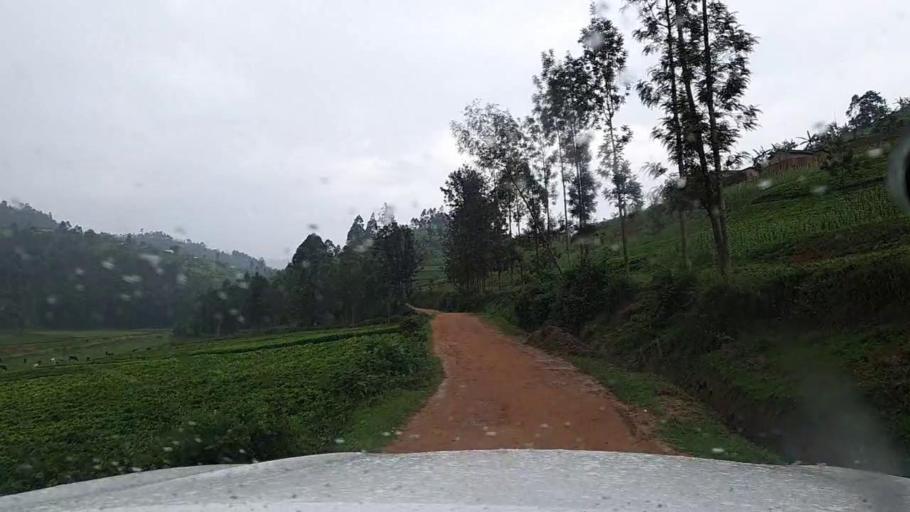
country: RW
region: Northern Province
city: Byumba
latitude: -1.6514
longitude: 29.9287
